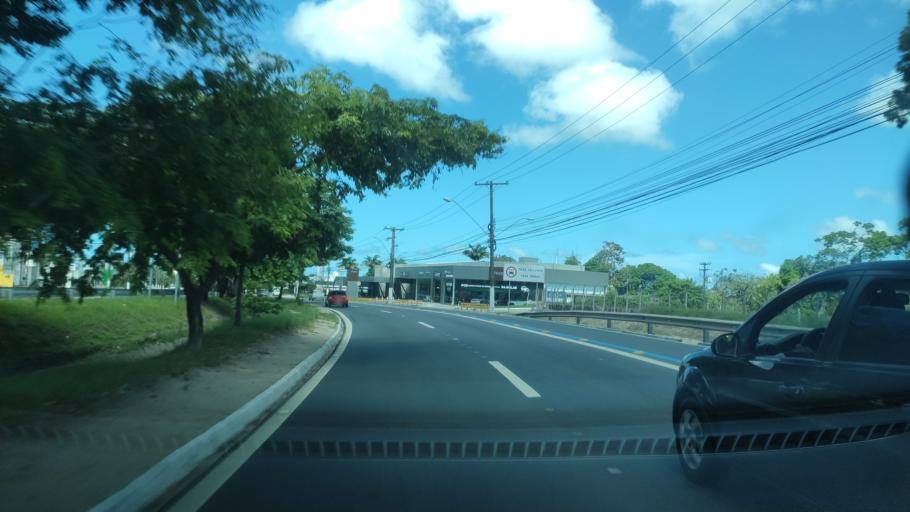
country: BR
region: Alagoas
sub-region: Maceio
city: Maceio
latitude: -9.6029
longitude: -35.7473
